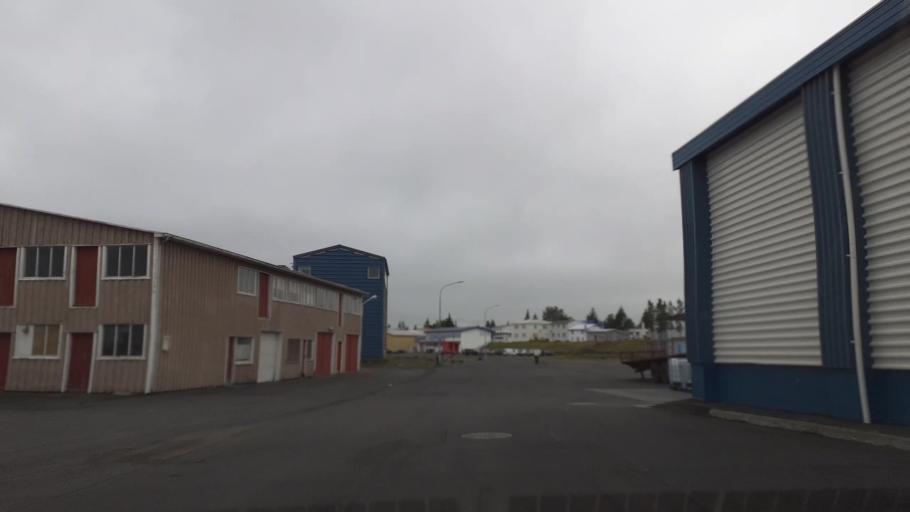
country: IS
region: Northeast
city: Dalvik
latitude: 65.9741
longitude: -18.5292
